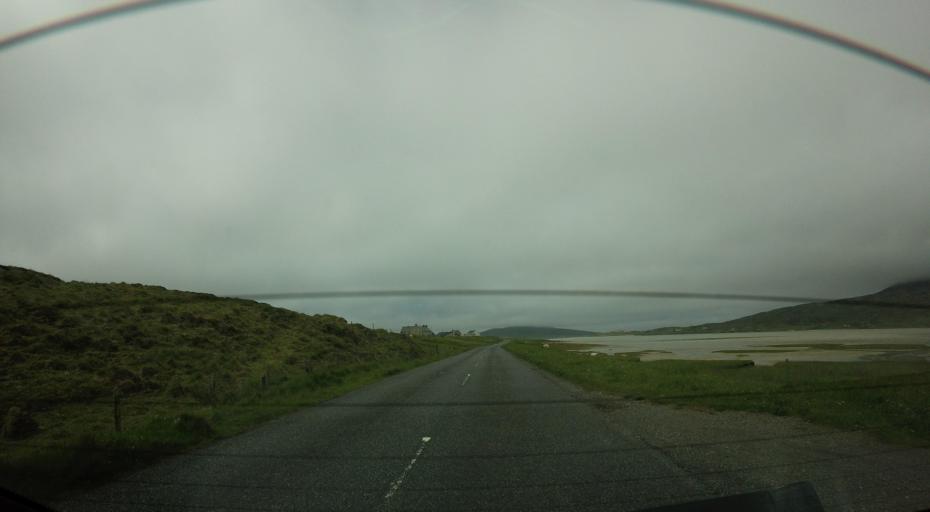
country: GB
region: Scotland
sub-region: Eilean Siar
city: Harris
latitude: 57.8670
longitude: -6.9281
